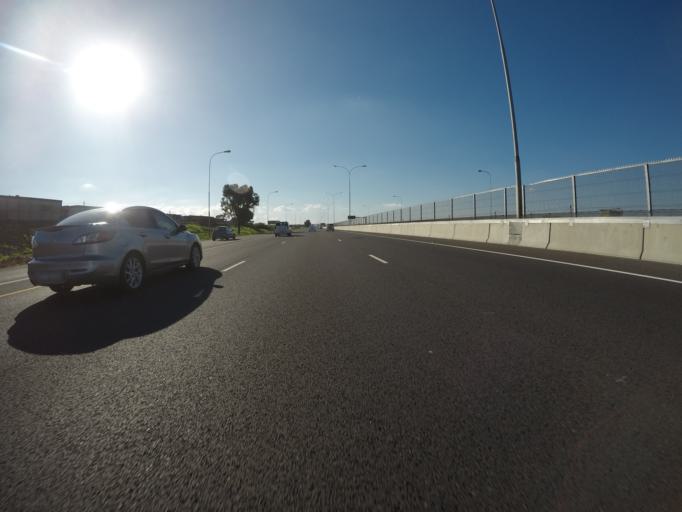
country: ZA
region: Western Cape
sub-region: City of Cape Town
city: Kraaifontein
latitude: -33.9749
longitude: 18.6531
